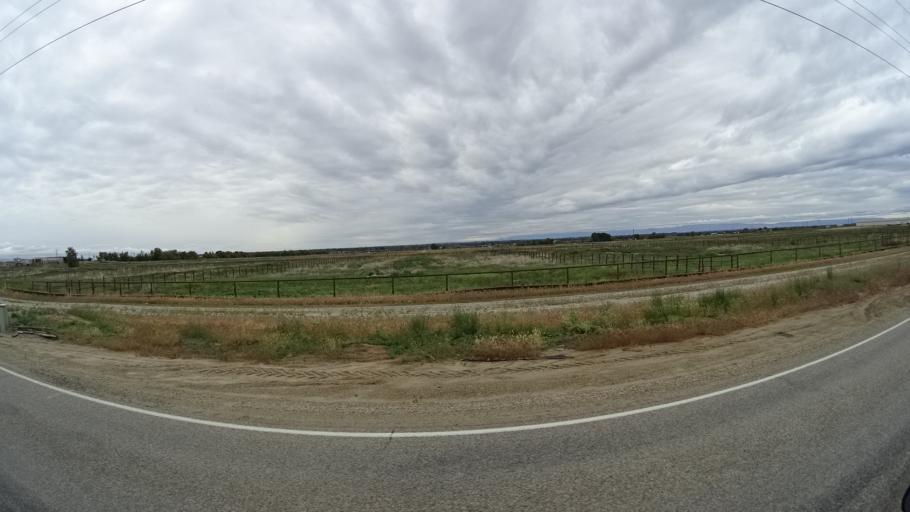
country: US
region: Idaho
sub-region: Ada County
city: Star
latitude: 43.7212
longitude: -116.4384
